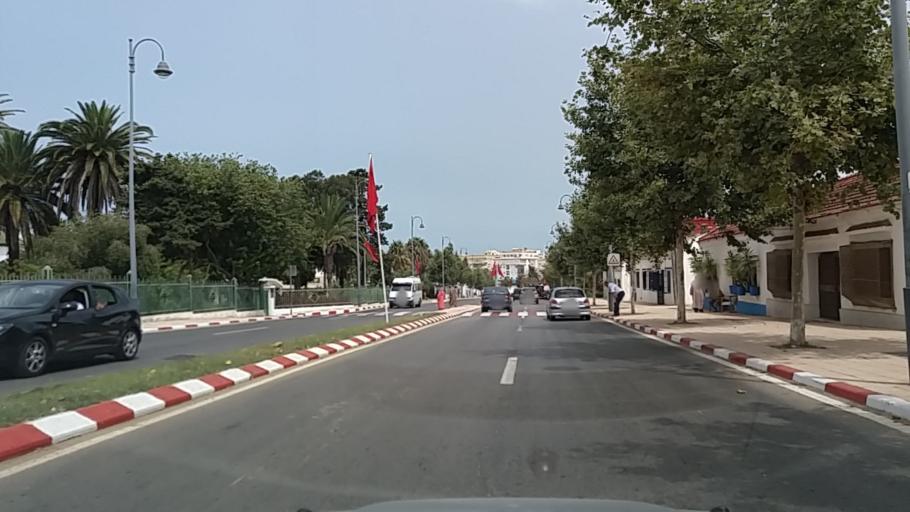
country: MA
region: Tanger-Tetouan
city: Asilah
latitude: 35.4669
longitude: -6.0304
